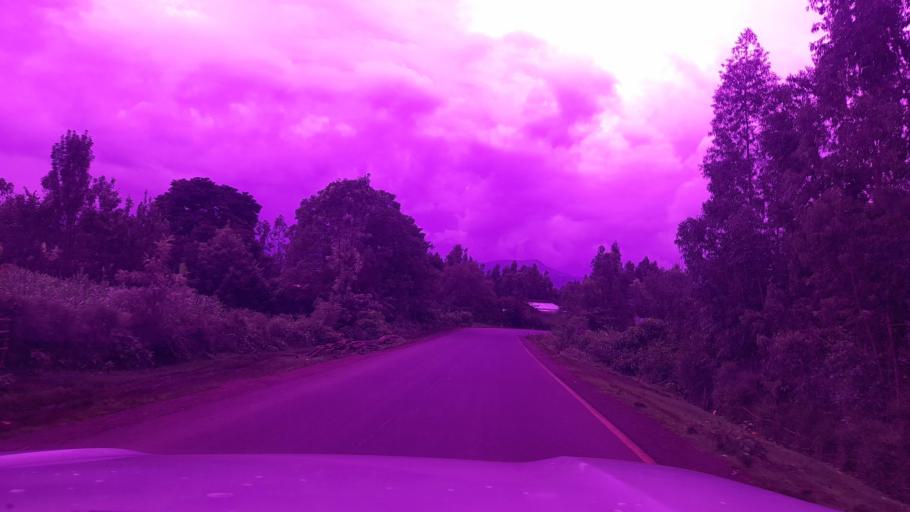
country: ET
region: Oromiya
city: Jima
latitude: 7.9162
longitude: 37.4043
